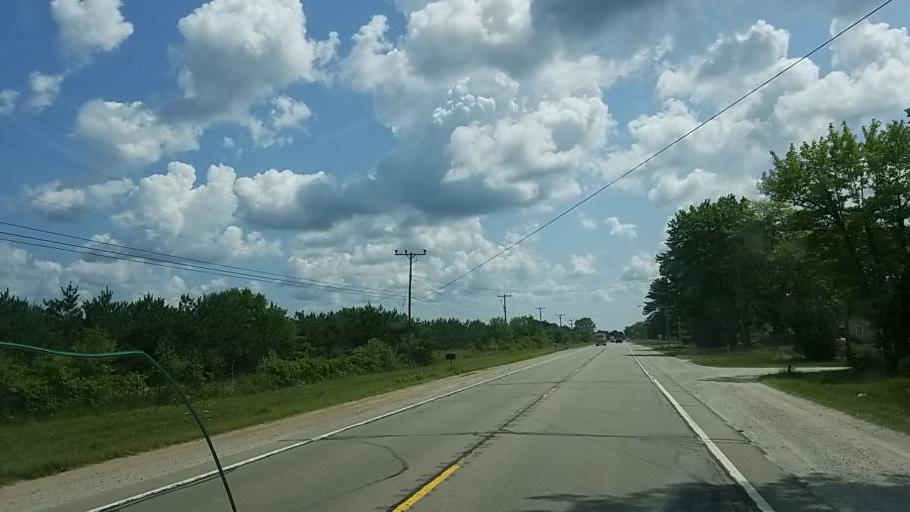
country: US
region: Michigan
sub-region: Muskegon County
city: Wolf Lake
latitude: 43.2353
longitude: -86.0354
